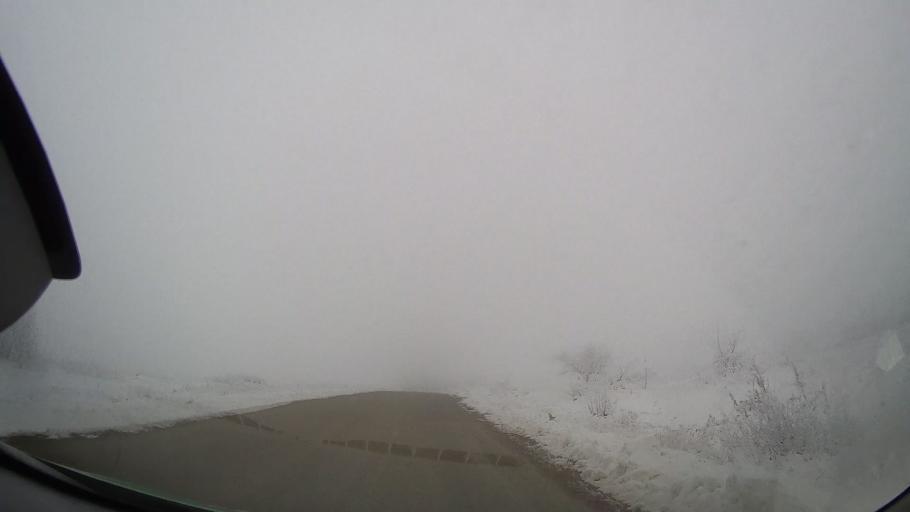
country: RO
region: Iasi
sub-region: Comuna Tansa
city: Suhulet
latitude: 46.8889
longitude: 27.2700
